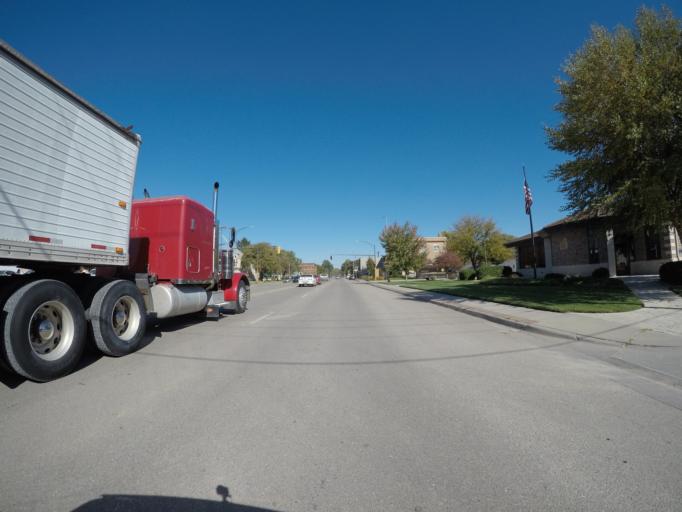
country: US
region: Kansas
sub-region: Clay County
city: Clay Center
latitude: 39.3757
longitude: -97.1245
